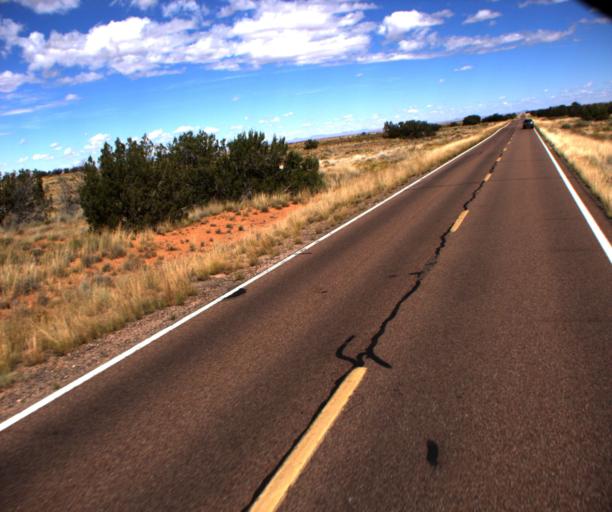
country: US
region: Arizona
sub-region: Navajo County
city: Holbrook
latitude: 34.6705
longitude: -110.3202
